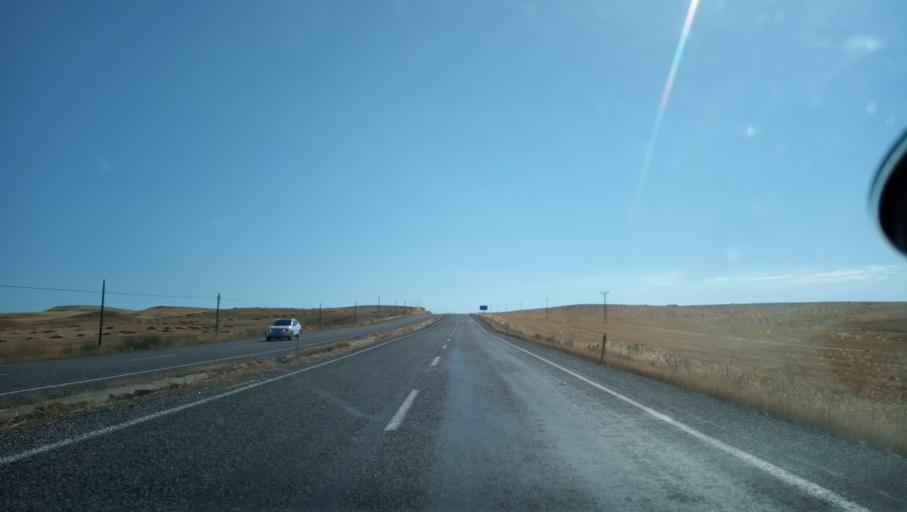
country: TR
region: Diyarbakir
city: Bagdere
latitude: 38.1272
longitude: 40.7518
